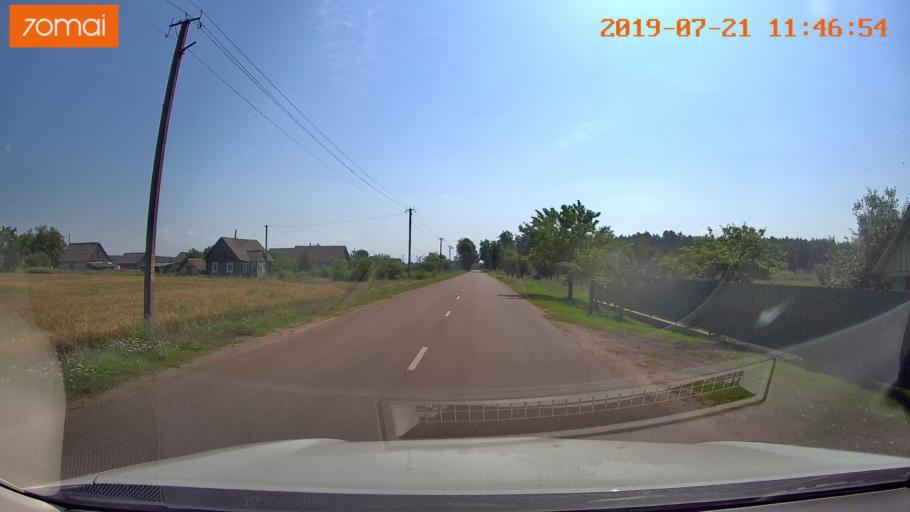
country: BY
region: Grodnenskaya
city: Lyubcha
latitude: 53.9052
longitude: 26.0382
